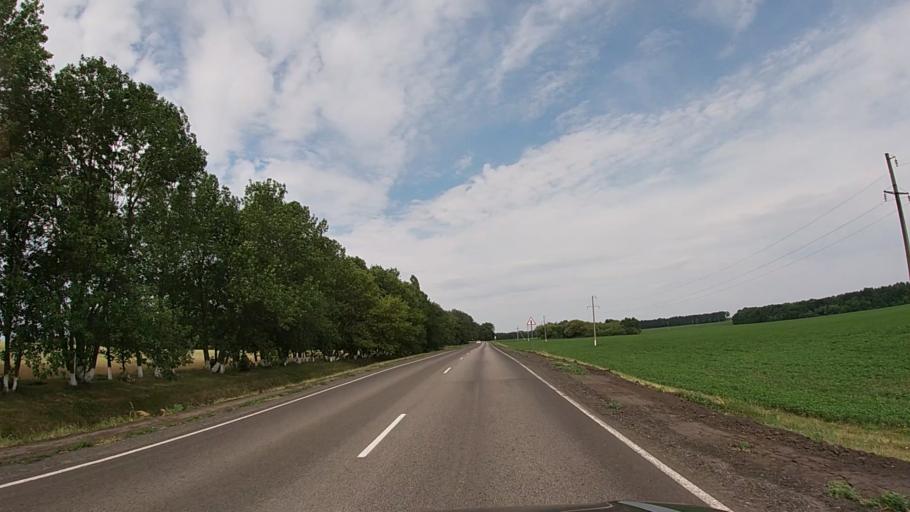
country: RU
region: Belgorod
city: Krasnaya Yaruga
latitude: 50.8102
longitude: 35.5162
